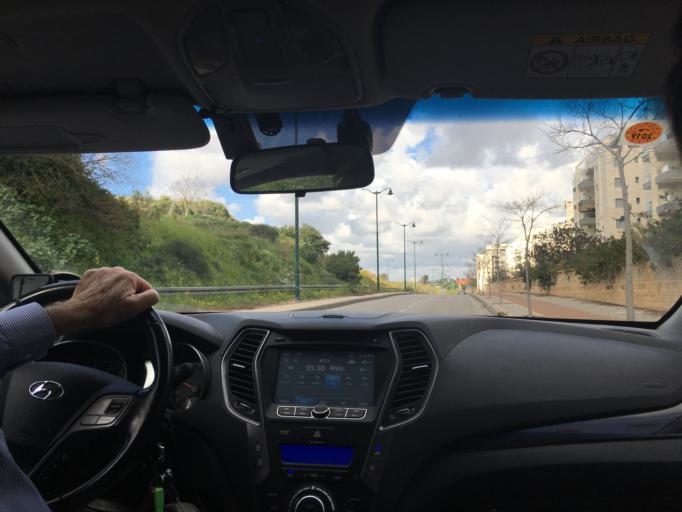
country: IL
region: Central District
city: Ness Ziona
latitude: 31.9295
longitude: 34.7846
